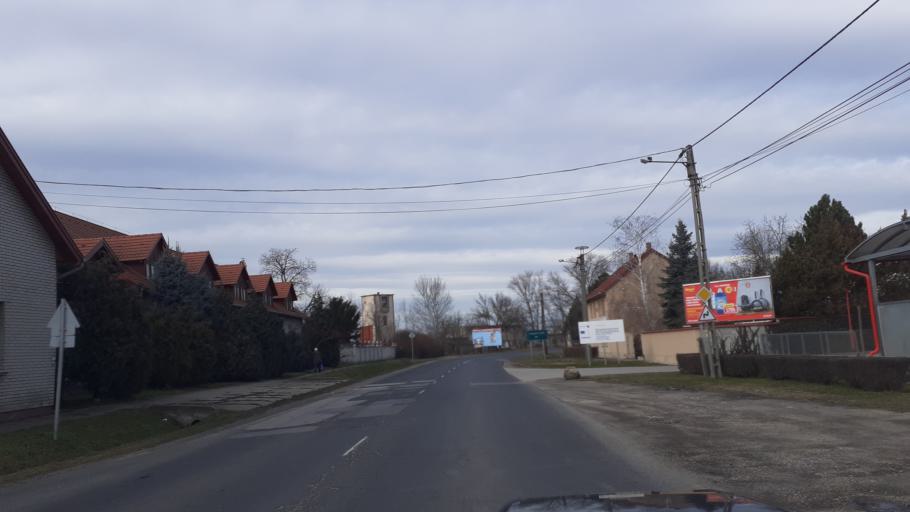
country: HU
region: Fejer
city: Sarbogard
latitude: 46.8980
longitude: 18.6143
